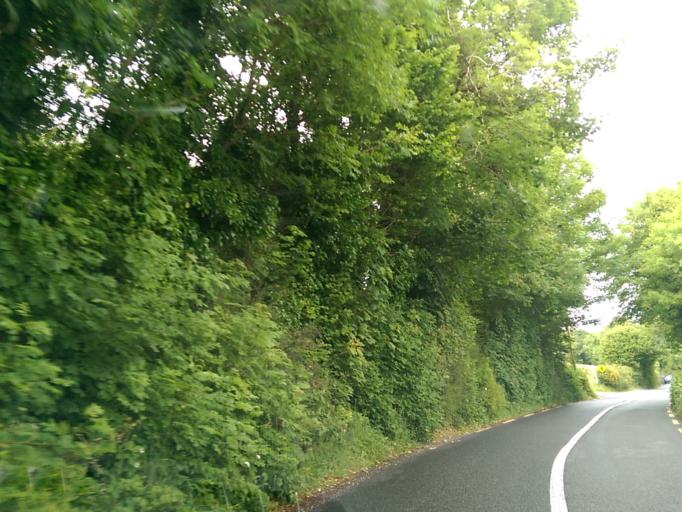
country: IE
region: Connaught
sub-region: County Galway
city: Bearna
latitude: 53.0728
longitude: -9.1881
